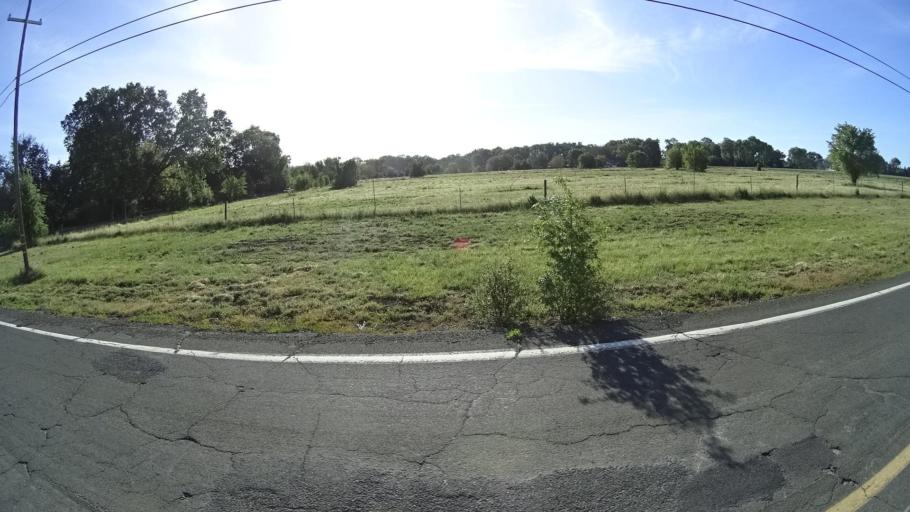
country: US
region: California
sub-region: Lake County
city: Lakeport
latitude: 39.0711
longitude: -122.9499
